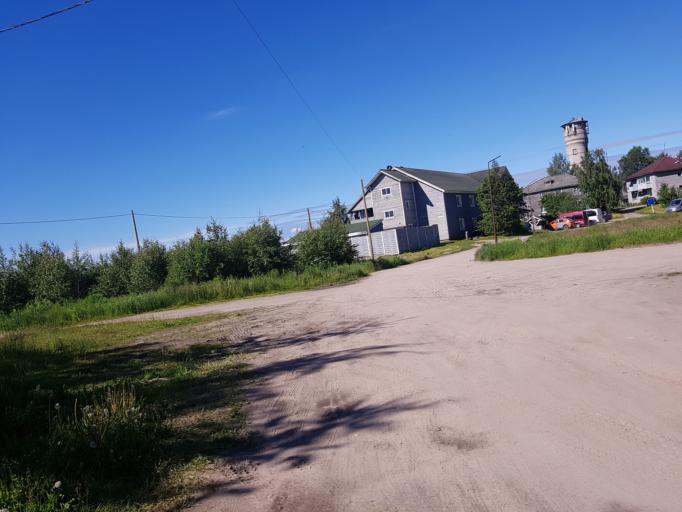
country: RU
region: Republic of Karelia
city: Kalevala
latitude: 65.1958
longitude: 31.2000
